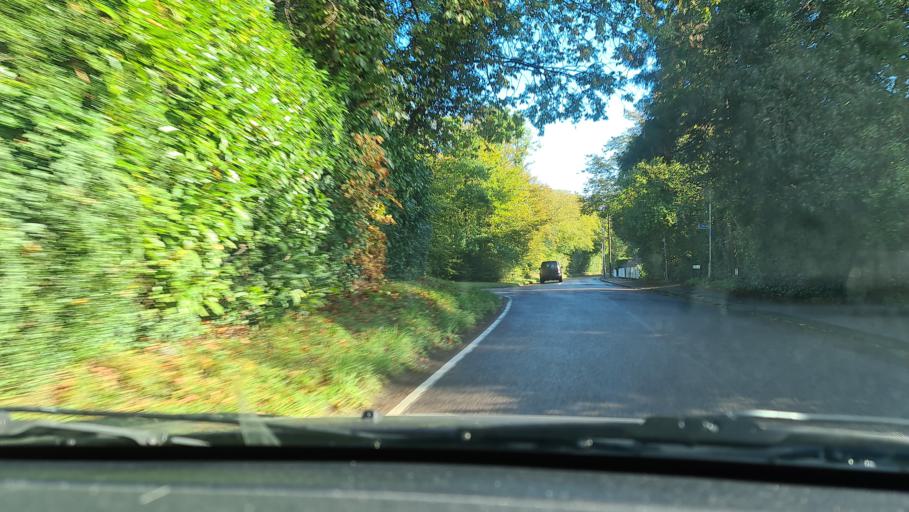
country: GB
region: England
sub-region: Buckinghamshire
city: Chalfont St Giles
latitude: 51.6498
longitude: -0.5297
